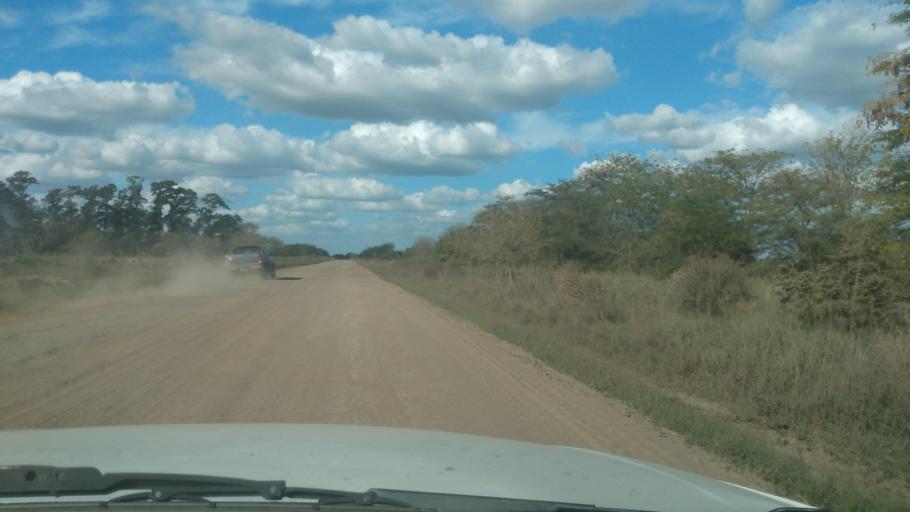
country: AR
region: Buenos Aires
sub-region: Partido de Navarro
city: Navarro
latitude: -35.0123
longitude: -59.4823
